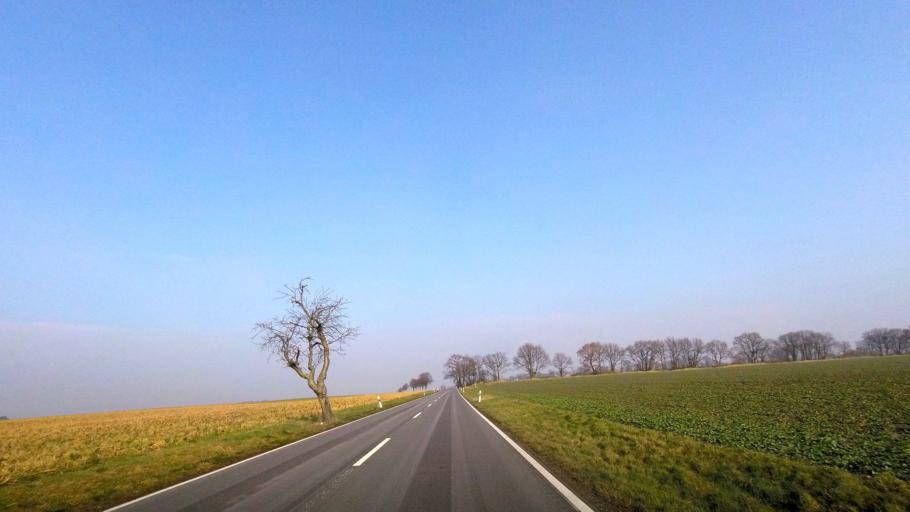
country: DE
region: Brandenburg
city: Niedergorsdorf
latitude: 51.9405
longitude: 13.0377
